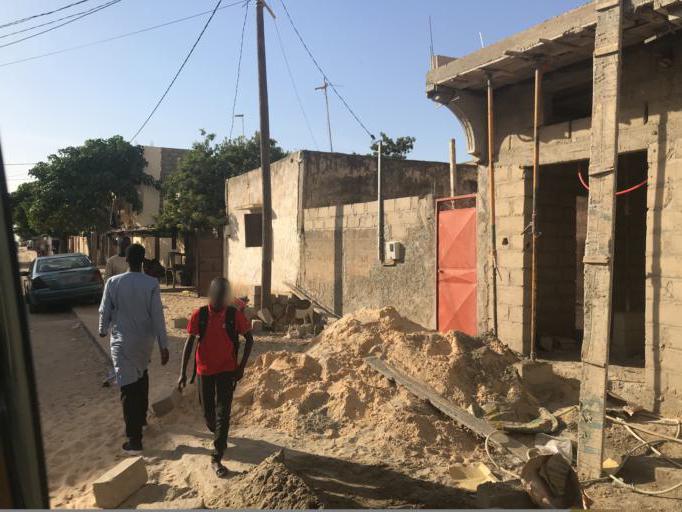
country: SN
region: Saint-Louis
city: Saint-Louis
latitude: 15.9934
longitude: -16.4896
